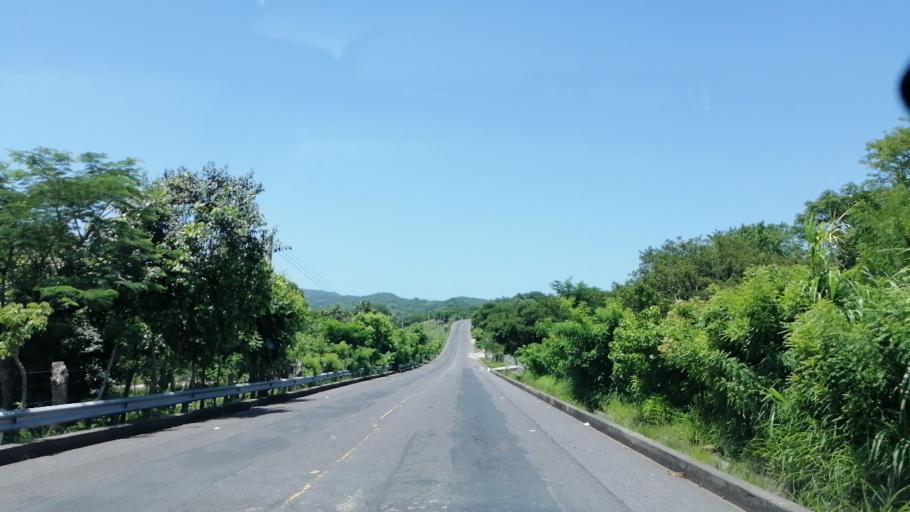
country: SV
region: Chalatenango
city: Chalatenango
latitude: 14.0303
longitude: -88.9472
